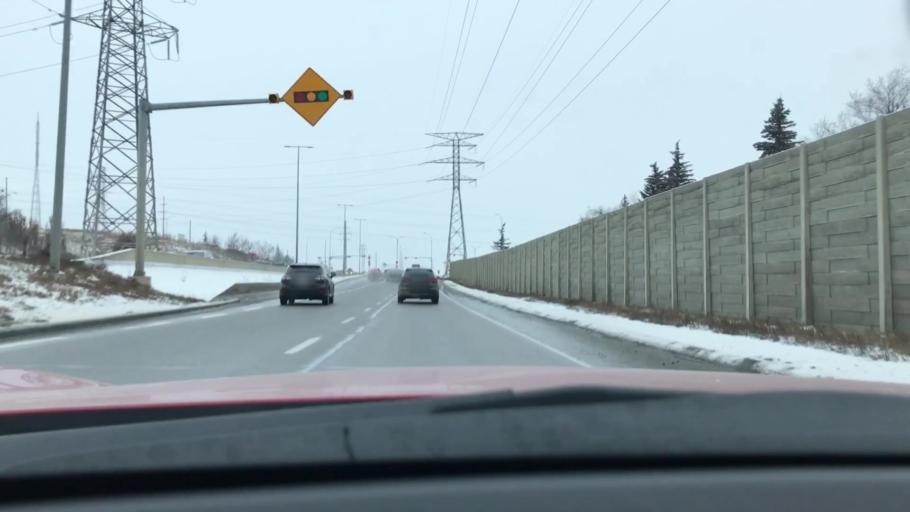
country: CA
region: Alberta
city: Calgary
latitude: 51.0500
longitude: -114.1642
